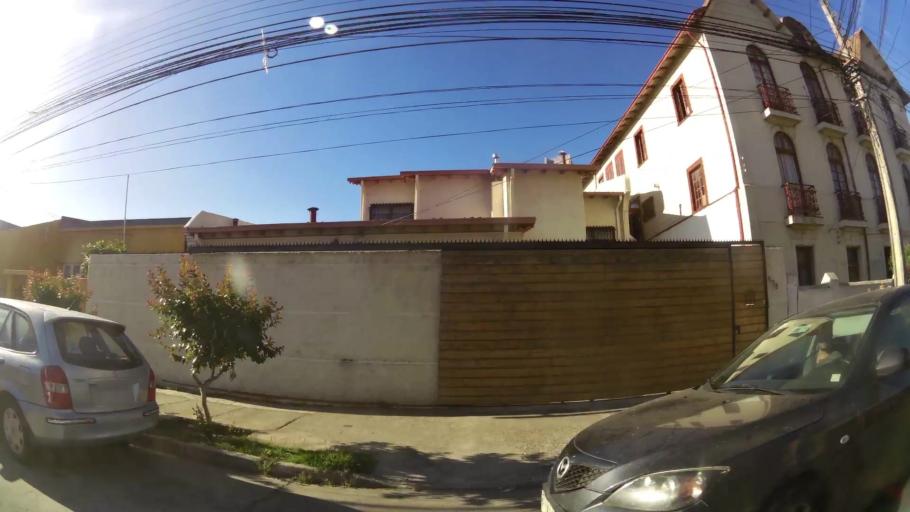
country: CL
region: Valparaiso
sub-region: Provincia de Valparaiso
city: Vina del Mar
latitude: -33.0300
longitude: -71.5693
